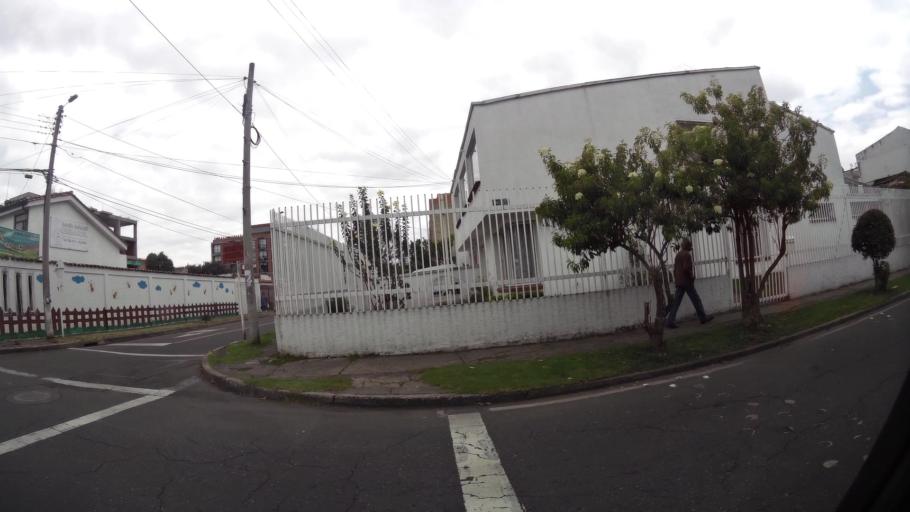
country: CO
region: Bogota D.C.
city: Barrio San Luis
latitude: 4.7164
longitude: -74.0703
